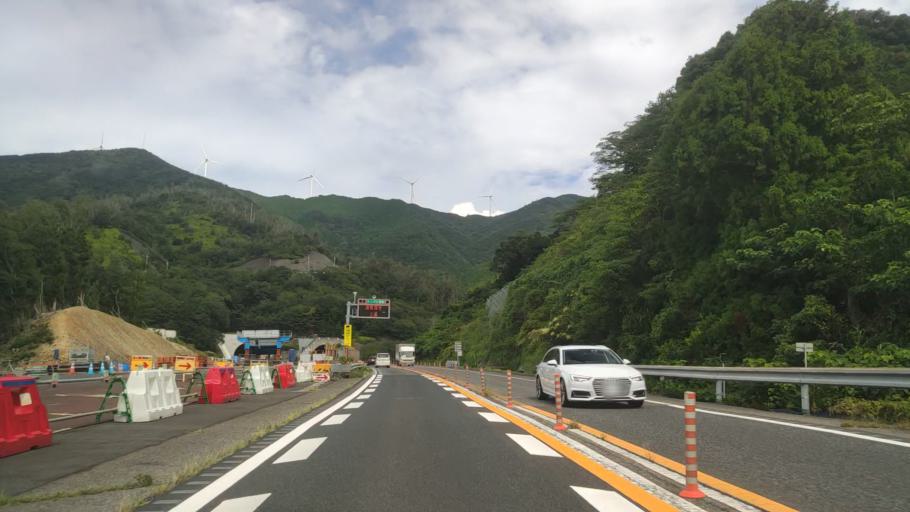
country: JP
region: Wakayama
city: Gobo
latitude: 33.9410
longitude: 135.1981
